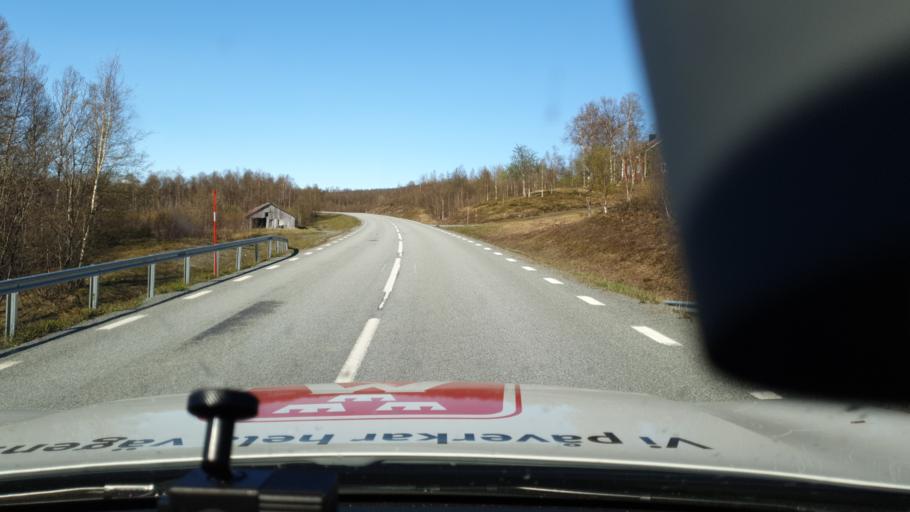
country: NO
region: Nordland
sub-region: Rana
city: Mo i Rana
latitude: 65.9729
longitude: 15.0601
